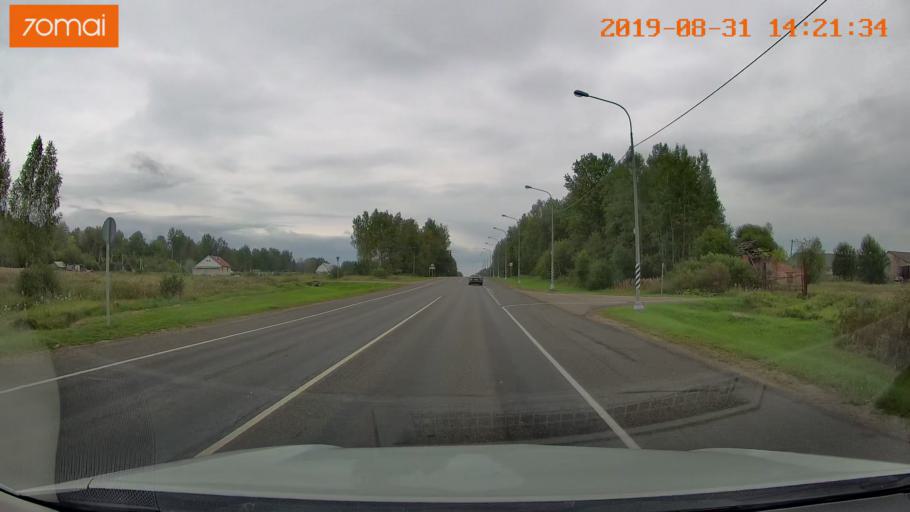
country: RU
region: Smolensk
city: Yekimovichi
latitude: 54.0863
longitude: 33.2001
